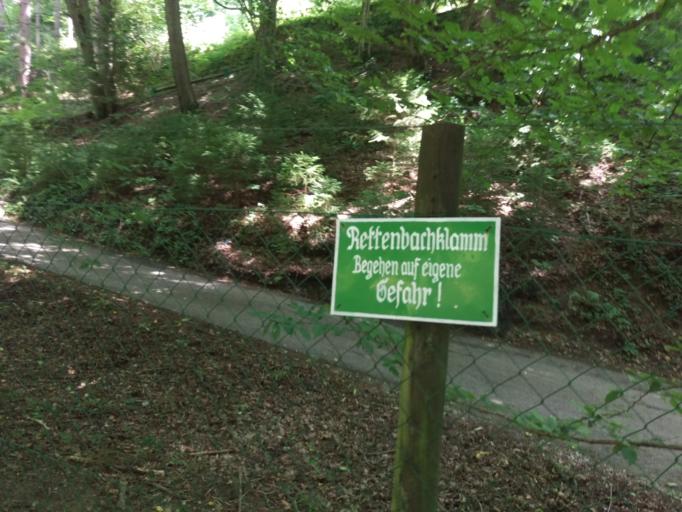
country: AT
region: Styria
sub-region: Graz Stadt
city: Mariatrost
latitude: 47.1051
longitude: 15.4778
